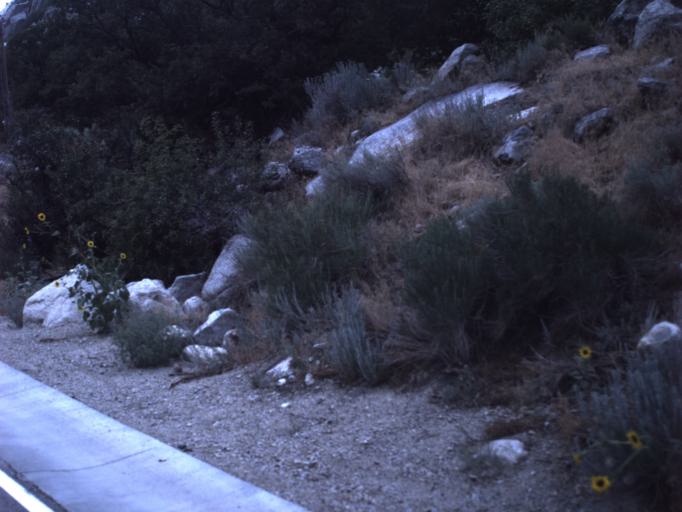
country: US
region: Utah
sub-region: Salt Lake County
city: Granite
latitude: 40.5718
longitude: -111.7624
